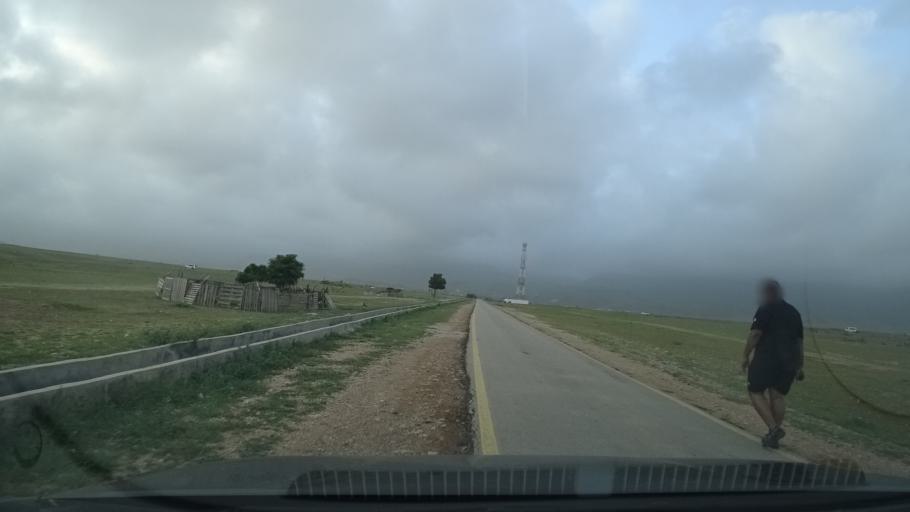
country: OM
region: Zufar
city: Salalah
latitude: 17.0834
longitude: 54.2318
